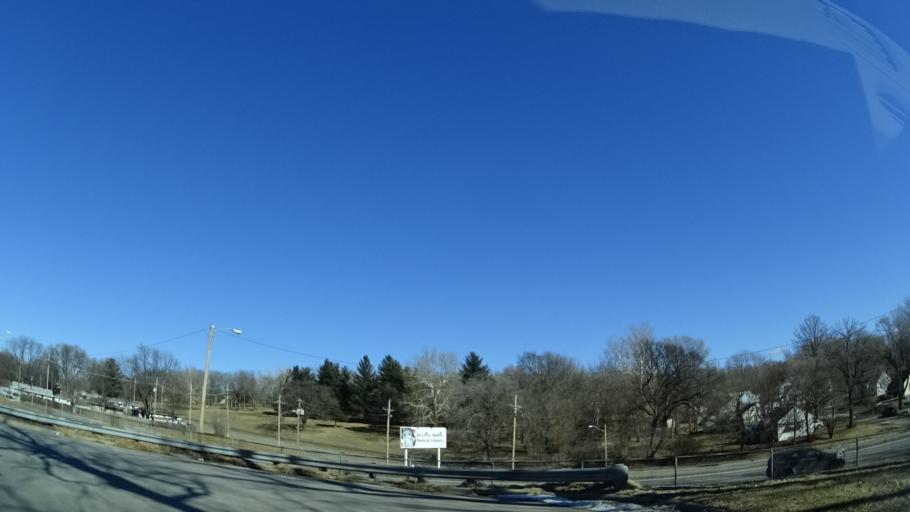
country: US
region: Nebraska
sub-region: Sarpy County
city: Bellevue
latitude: 41.1390
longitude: -95.9082
